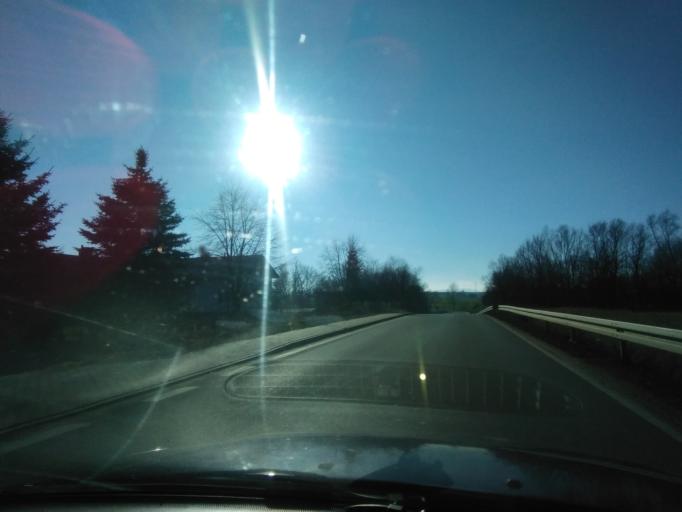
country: PL
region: Subcarpathian Voivodeship
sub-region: Powiat krosnienski
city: Kroscienko Wyzne
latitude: 49.6782
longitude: 21.8654
